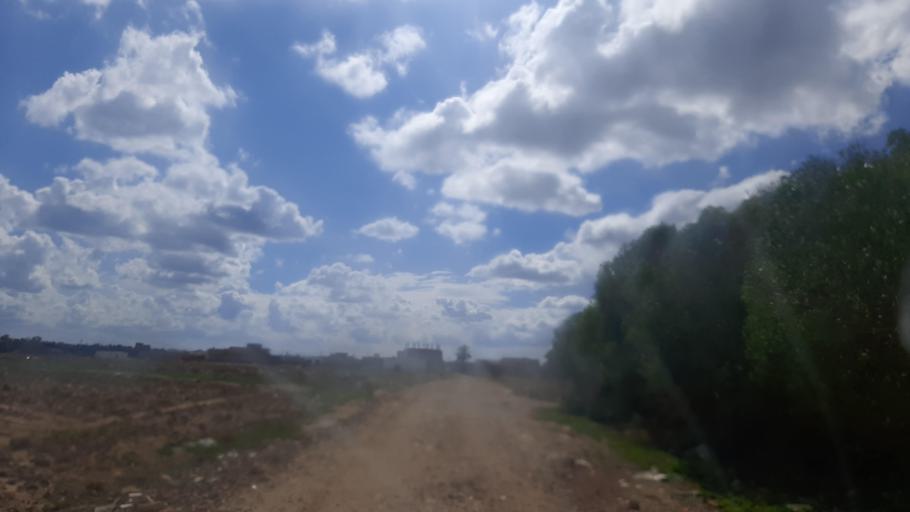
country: TN
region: Nabul
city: Korba
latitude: 36.5979
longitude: 10.8564
